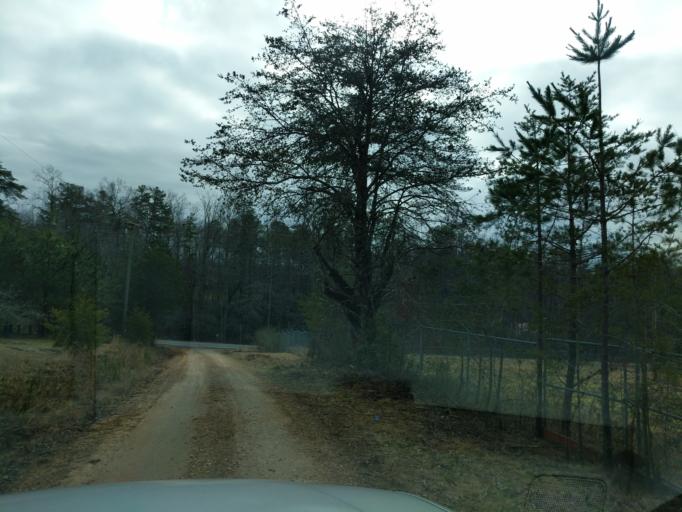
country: US
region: Georgia
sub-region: Rabun County
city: Clayton
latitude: 34.7945
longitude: -83.2431
